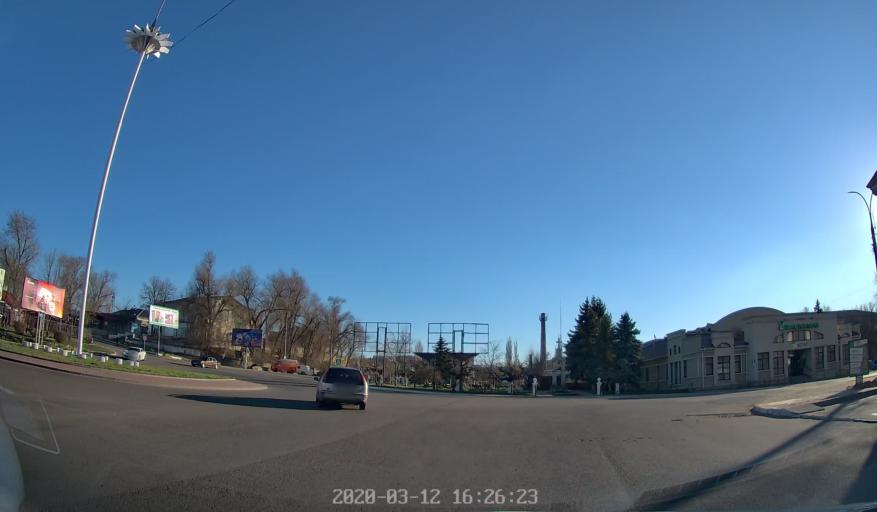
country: MD
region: Anenii Noi
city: Anenii Noi
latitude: 46.8818
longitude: 29.2325
